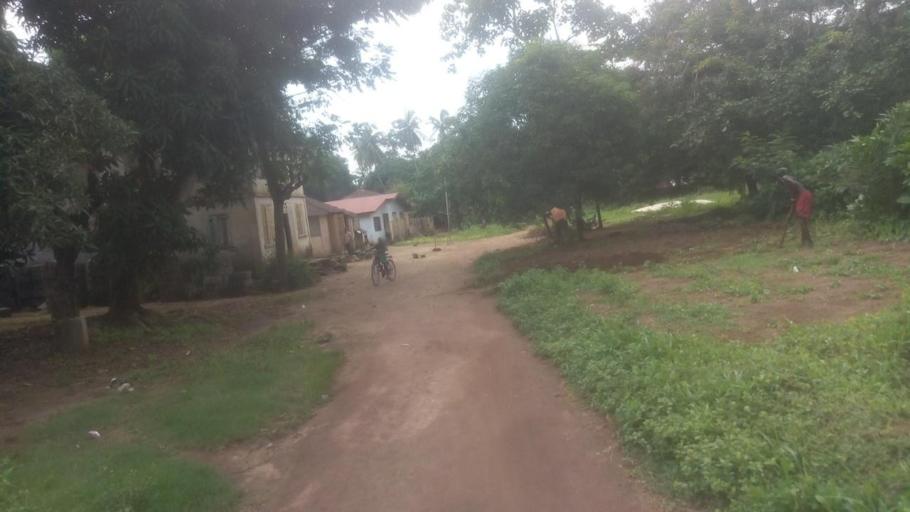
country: SL
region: Northern Province
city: Tintafor
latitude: 8.6432
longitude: -13.2271
